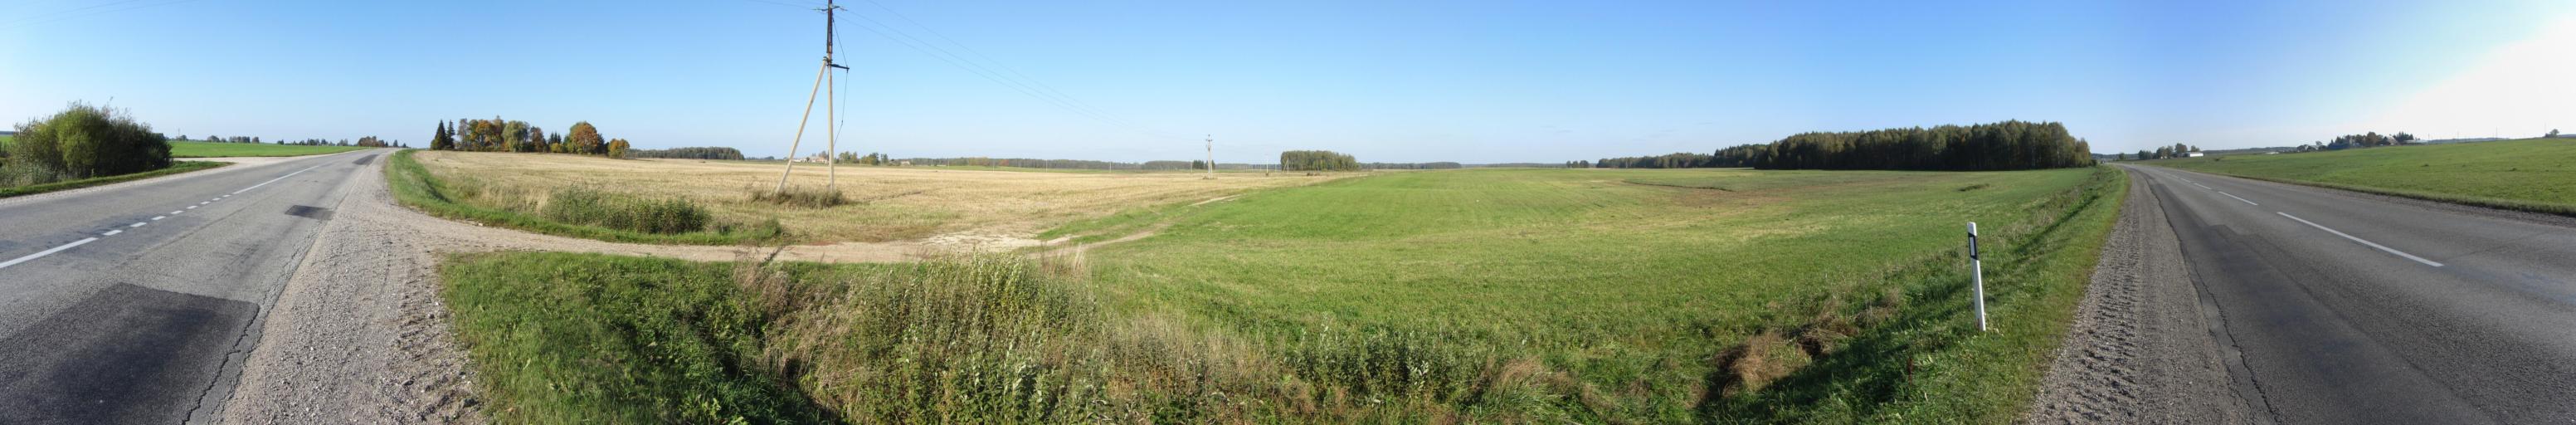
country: LT
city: Obeliai
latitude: 55.9951
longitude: 25.2570
